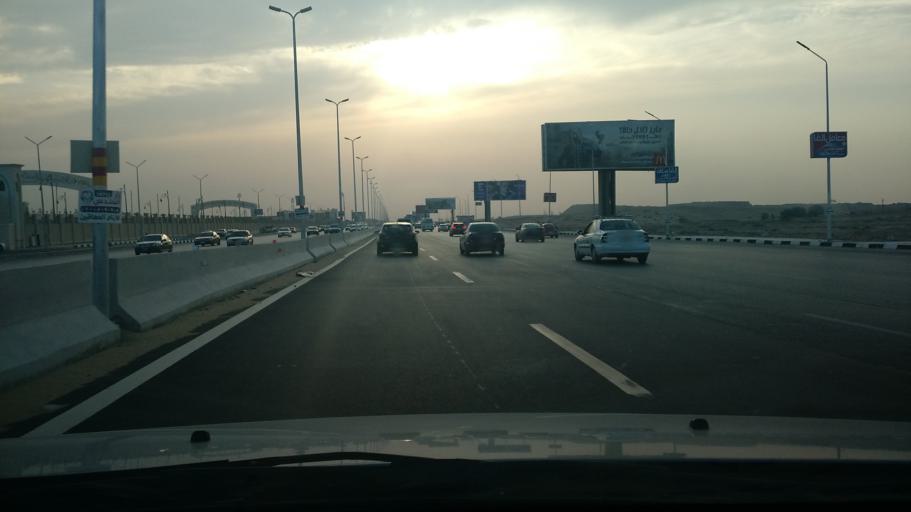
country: EG
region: Muhafazat al Qahirah
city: Cairo
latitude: 30.0182
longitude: 31.3871
